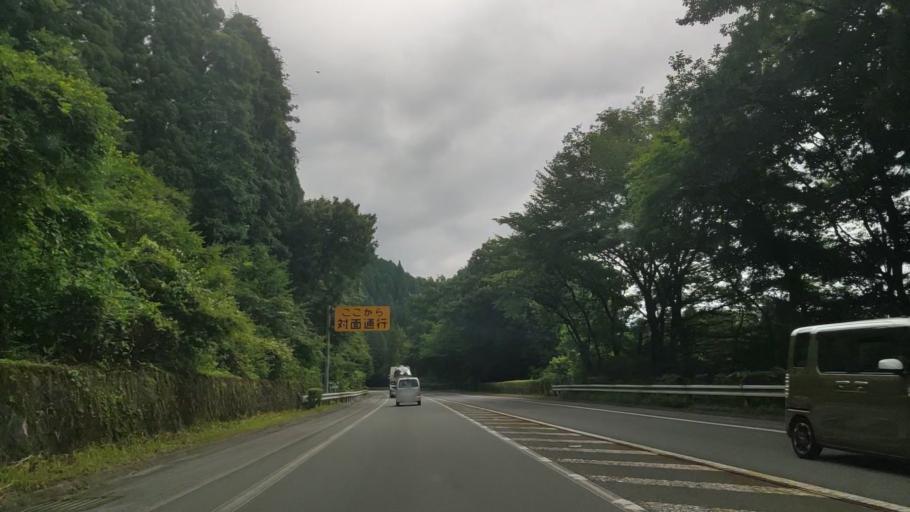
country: JP
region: Tochigi
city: Nikko
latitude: 36.7428
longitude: 139.6202
